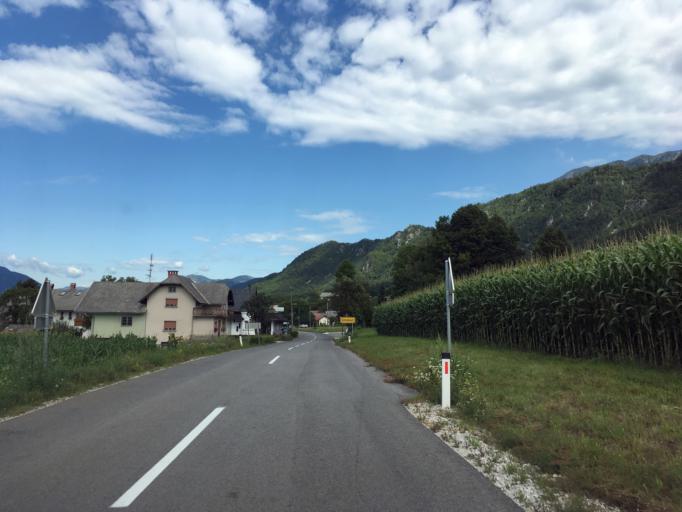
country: SI
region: Radovljica
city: Lesce
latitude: 46.3861
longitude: 14.1711
